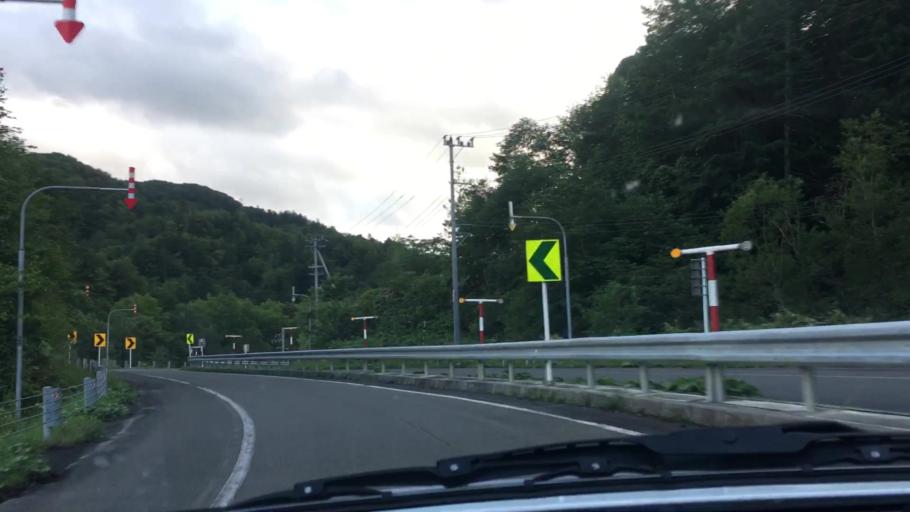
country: JP
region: Hokkaido
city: Shimo-furano
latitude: 43.0467
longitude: 142.4723
